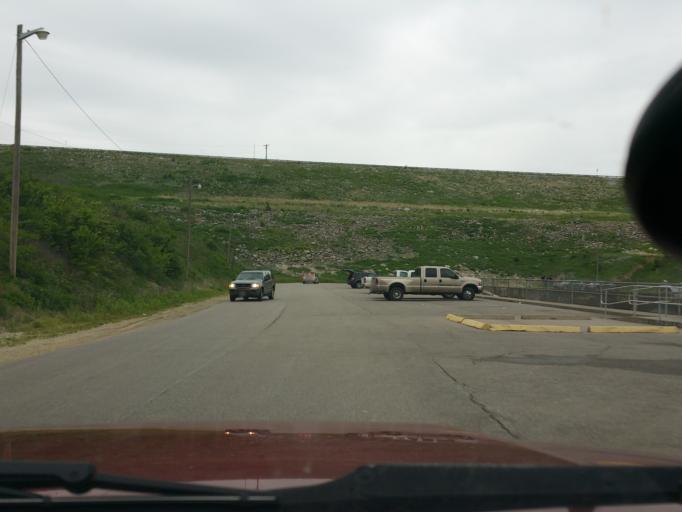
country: US
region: Kansas
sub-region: Riley County
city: Manhattan
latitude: 39.2514
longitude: -96.6006
